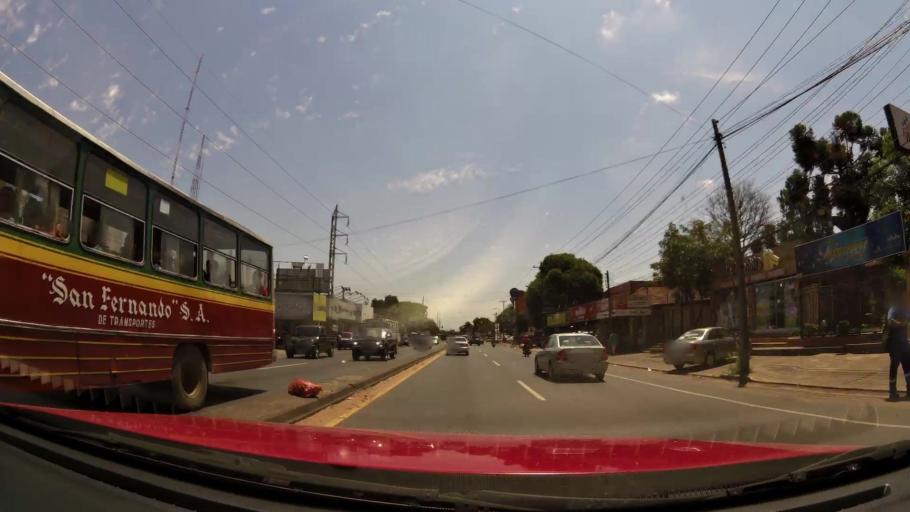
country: PY
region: Central
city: Villa Elisa
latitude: -25.3485
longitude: -57.5751
